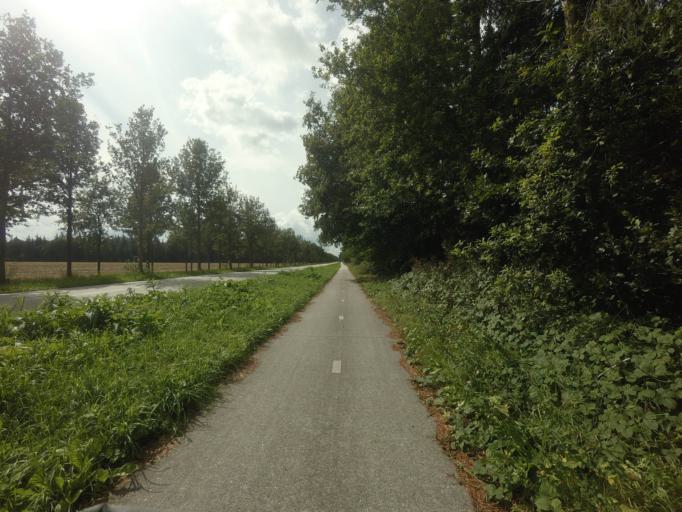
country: NL
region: Groningen
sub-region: Gemeente Leek
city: Leek
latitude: 53.0298
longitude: 6.4181
